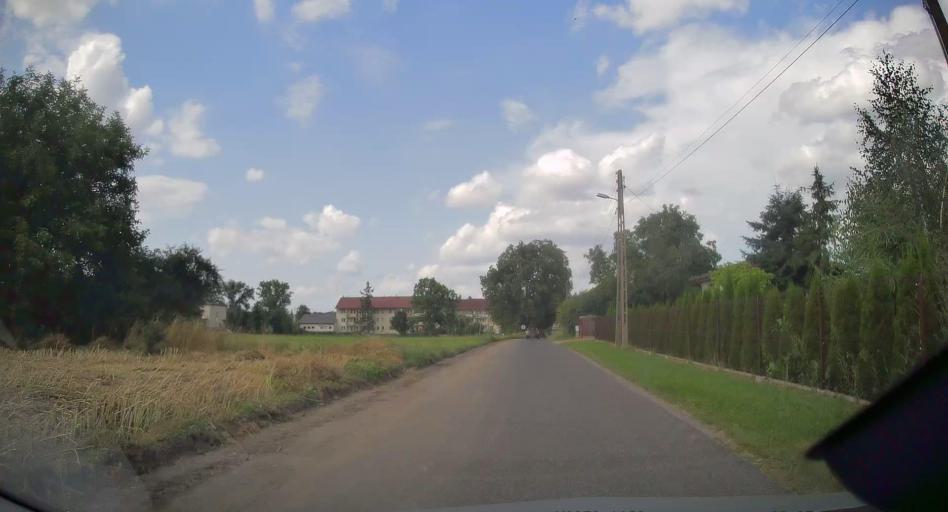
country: PL
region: Lodz Voivodeship
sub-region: Powiat brzezinski
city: Rogow
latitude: 51.8161
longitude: 19.8971
